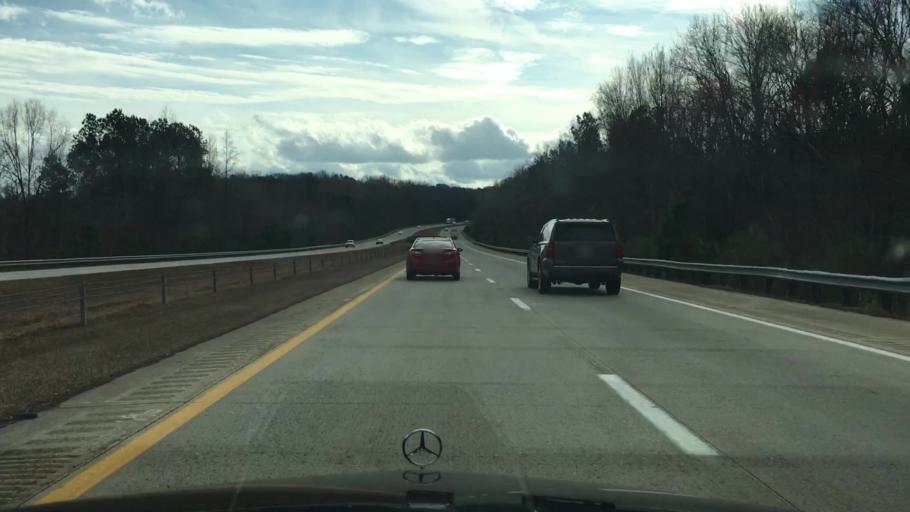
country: US
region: North Carolina
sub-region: Johnston County
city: Clayton
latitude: 35.5651
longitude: -78.5761
